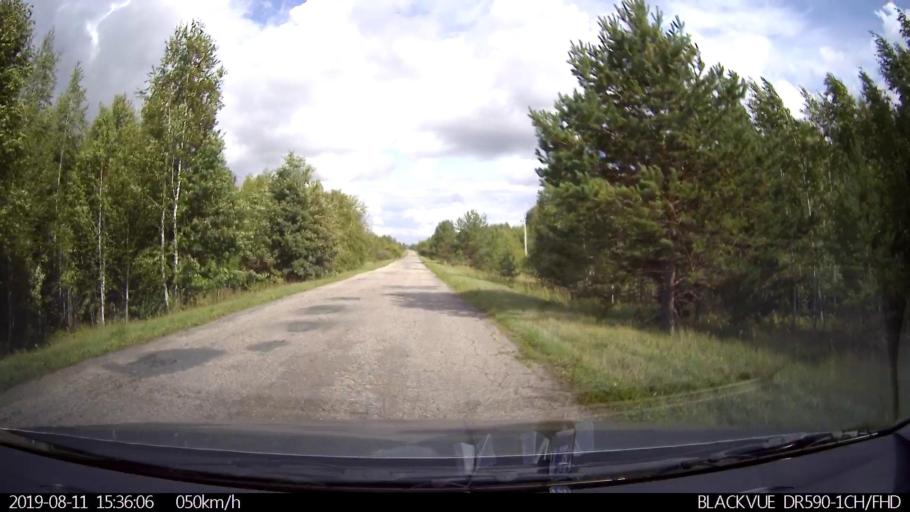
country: RU
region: Ulyanovsk
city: Ignatovka
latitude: 53.8596
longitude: 47.6160
